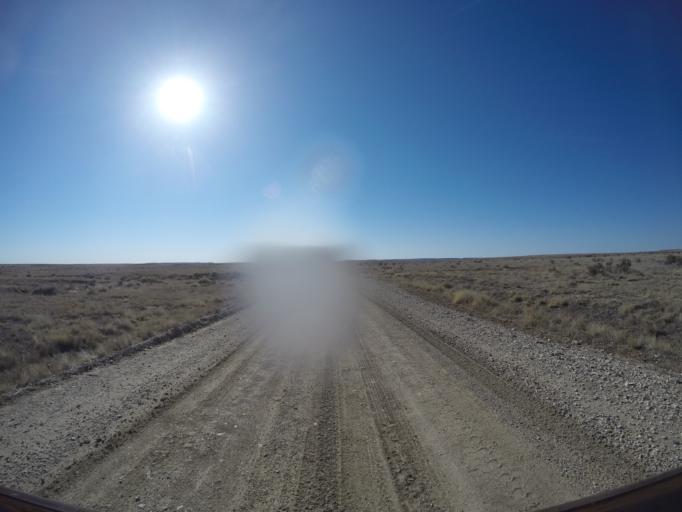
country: US
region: Colorado
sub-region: Otero County
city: La Junta
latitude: 37.7154
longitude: -103.6206
